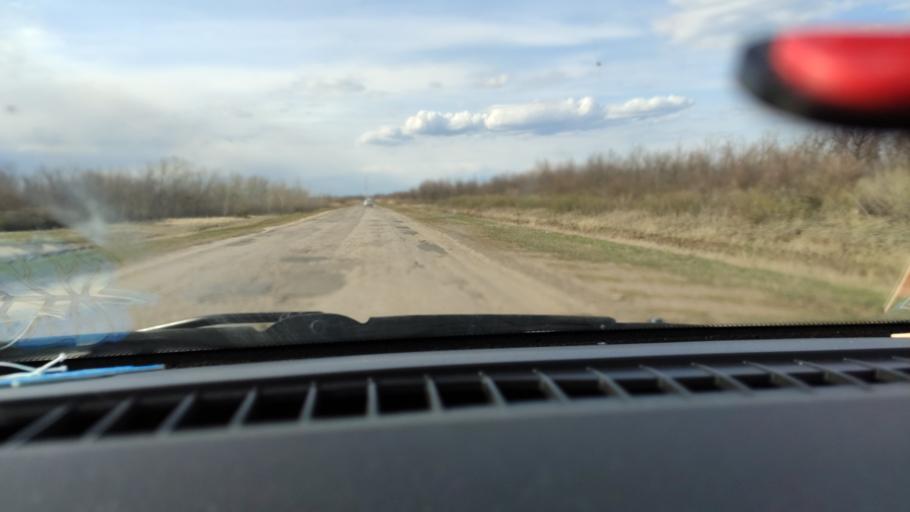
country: RU
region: Saratov
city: Rovnoye
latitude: 51.0071
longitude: 46.1005
